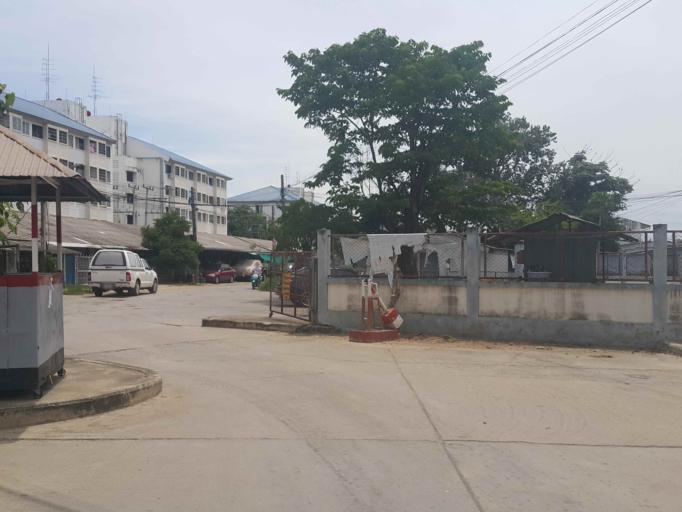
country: TH
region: Chiang Mai
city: Chiang Mai
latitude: 18.7604
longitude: 99.0143
